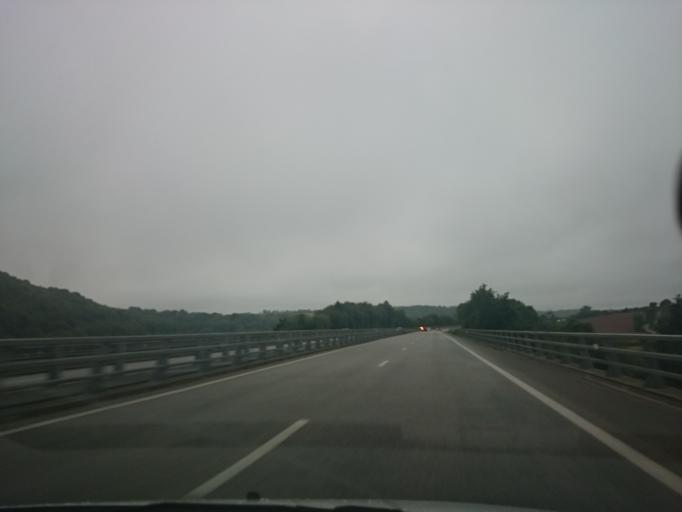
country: FR
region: Brittany
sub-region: Departement du Finistere
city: Chateaulin
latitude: 48.1811
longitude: -4.0453
